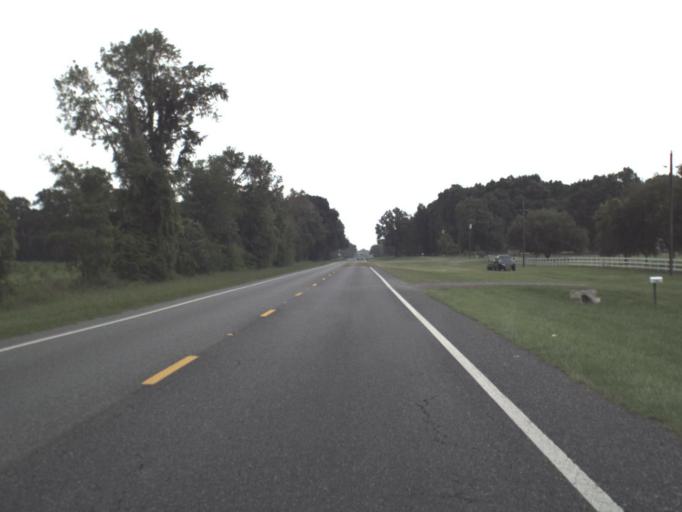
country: US
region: Florida
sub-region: Alachua County
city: High Springs
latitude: 29.8943
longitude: -82.6092
